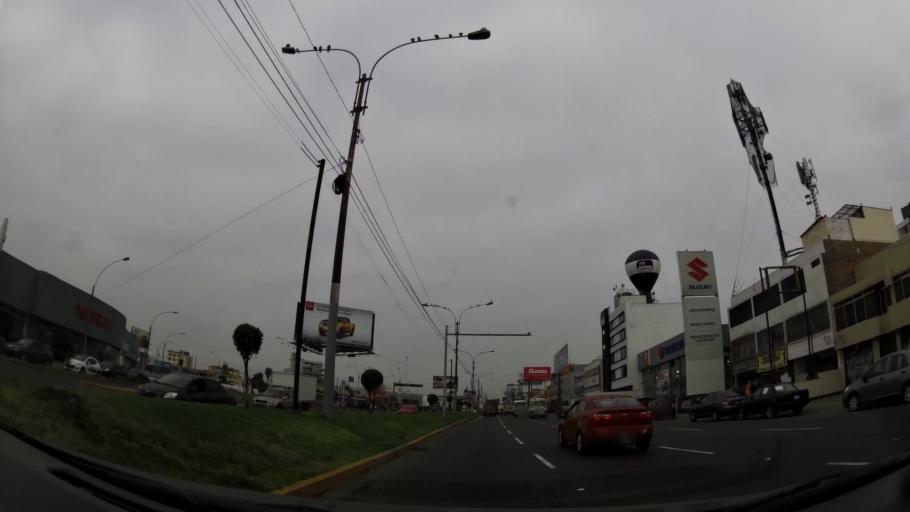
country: PE
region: Callao
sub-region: Callao
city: Callao
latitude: -12.0738
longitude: -77.1011
